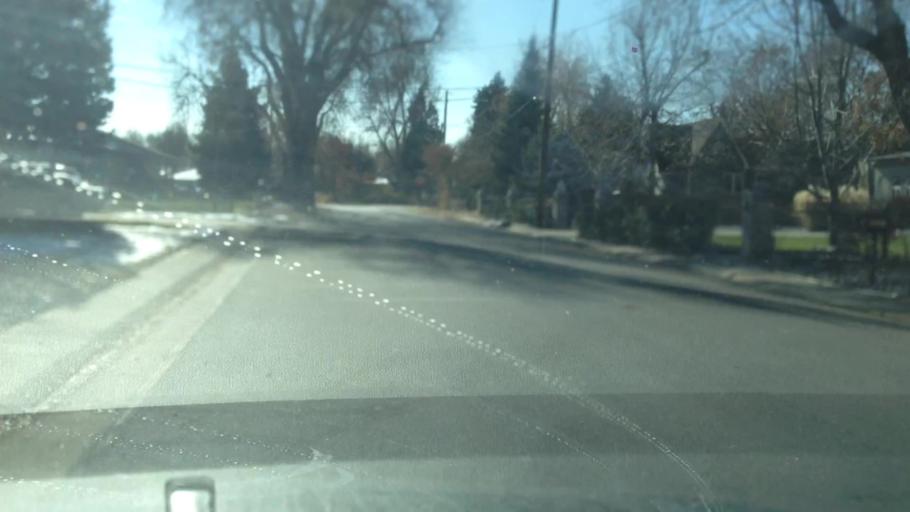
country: US
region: Colorado
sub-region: Jefferson County
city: Lakewood
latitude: 39.7239
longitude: -105.0755
